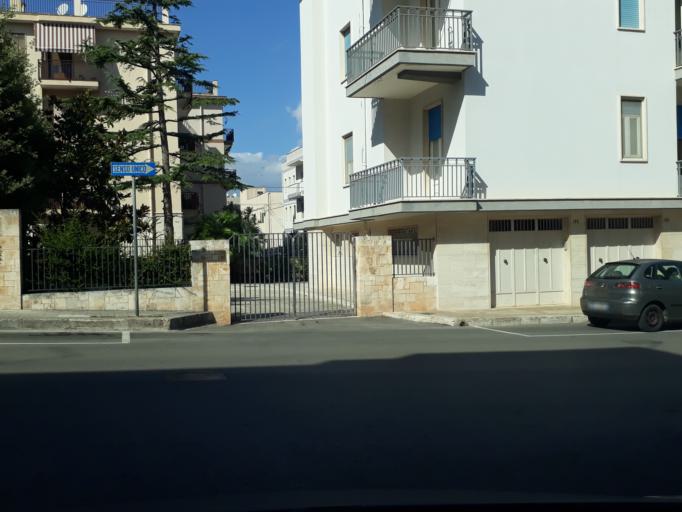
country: IT
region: Apulia
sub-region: Provincia di Brindisi
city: Fasano
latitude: 40.8302
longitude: 17.3546
